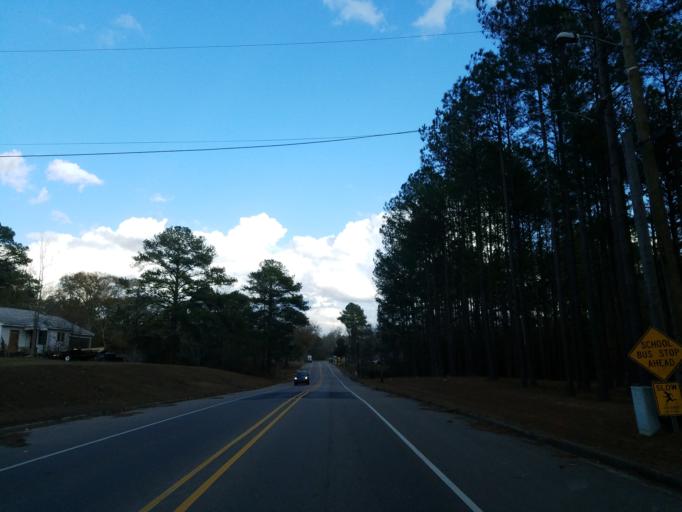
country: US
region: Mississippi
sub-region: Jones County
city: Sharon
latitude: 31.7880
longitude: -89.0400
